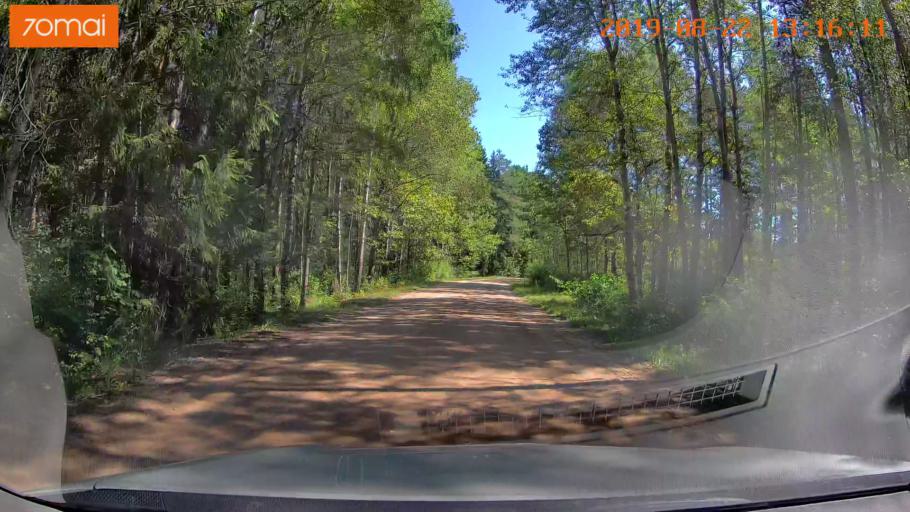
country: BY
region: Minsk
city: Prawdzinski
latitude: 53.2570
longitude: 27.9082
